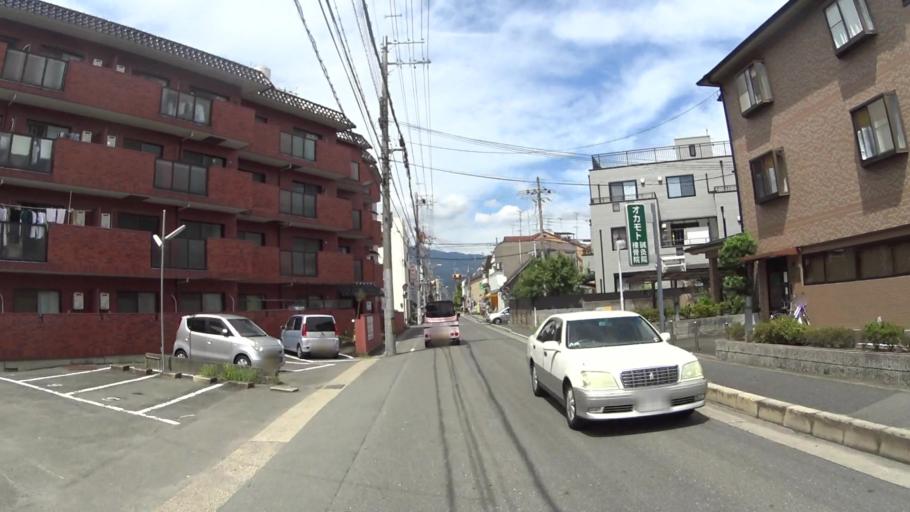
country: JP
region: Kyoto
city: Muko
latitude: 35.0026
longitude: 135.6861
